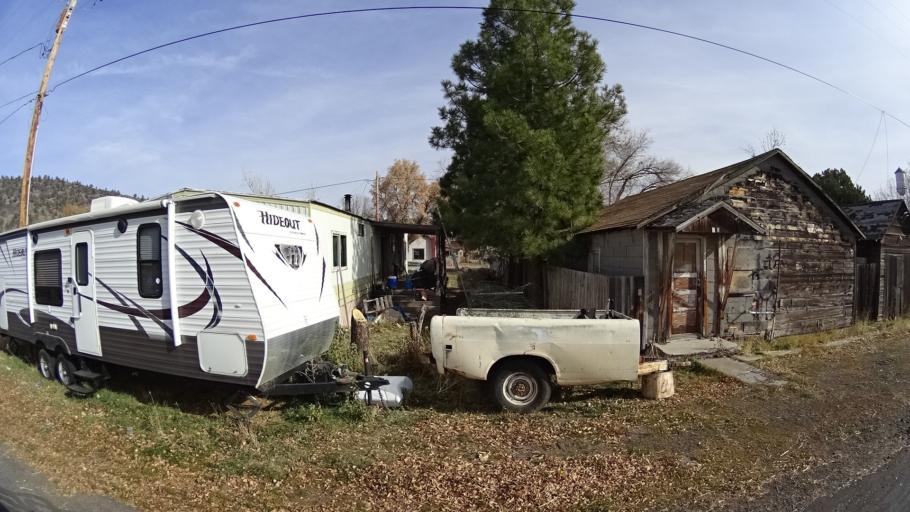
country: US
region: Oregon
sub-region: Klamath County
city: Klamath Falls
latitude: 41.9680
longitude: -121.9213
